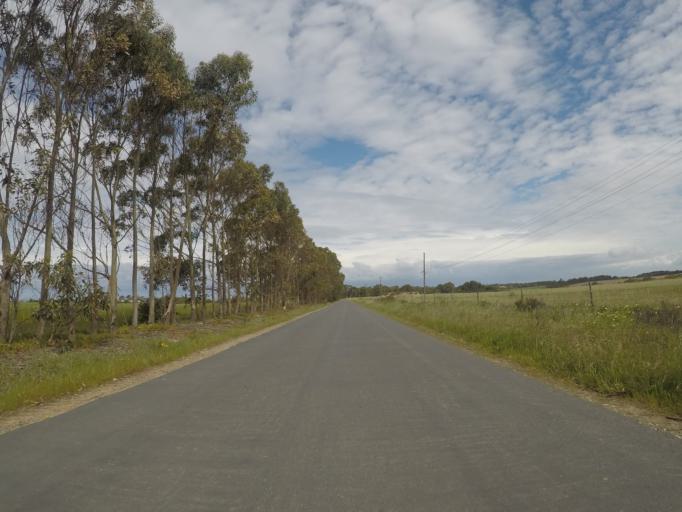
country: PT
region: Beja
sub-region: Odemira
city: Sao Teotonio
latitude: 37.4921
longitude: -8.7824
